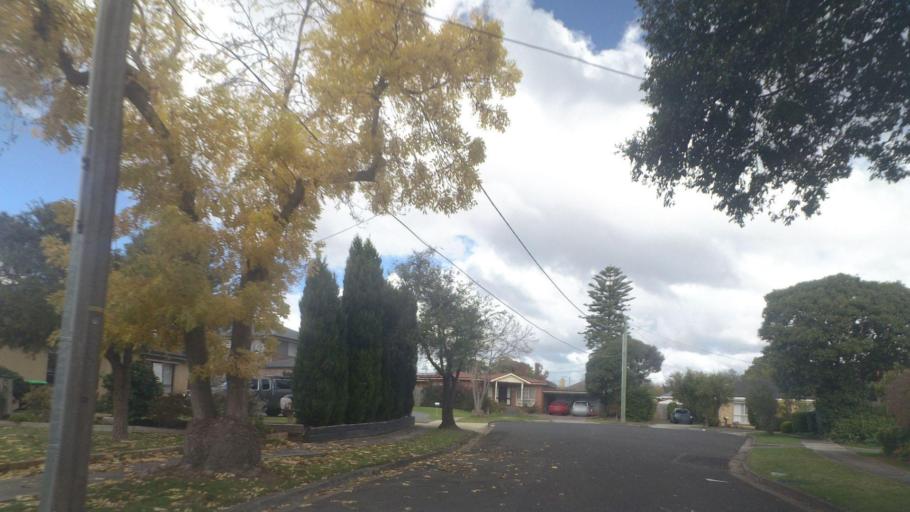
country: AU
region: Victoria
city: Forest Hill
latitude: -37.8411
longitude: 145.1783
